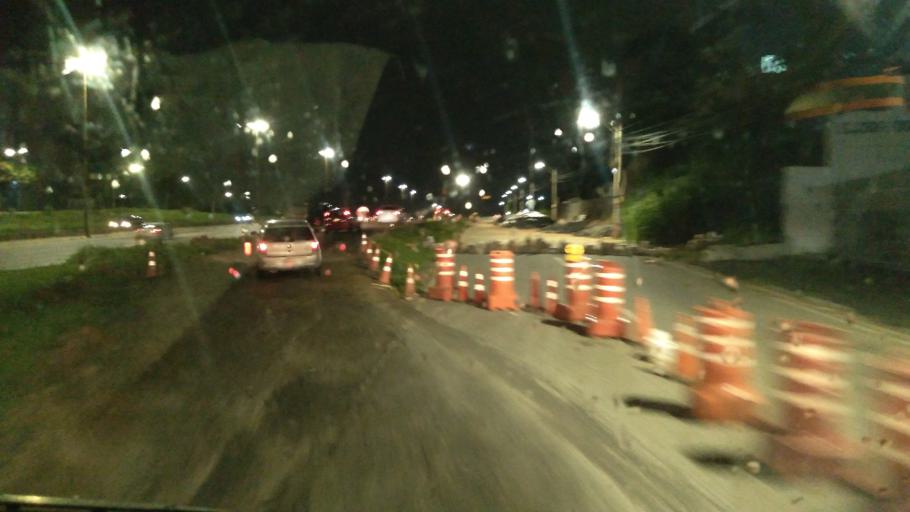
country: BR
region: Minas Gerais
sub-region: Belo Horizonte
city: Belo Horizonte
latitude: -19.9025
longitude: -43.9846
